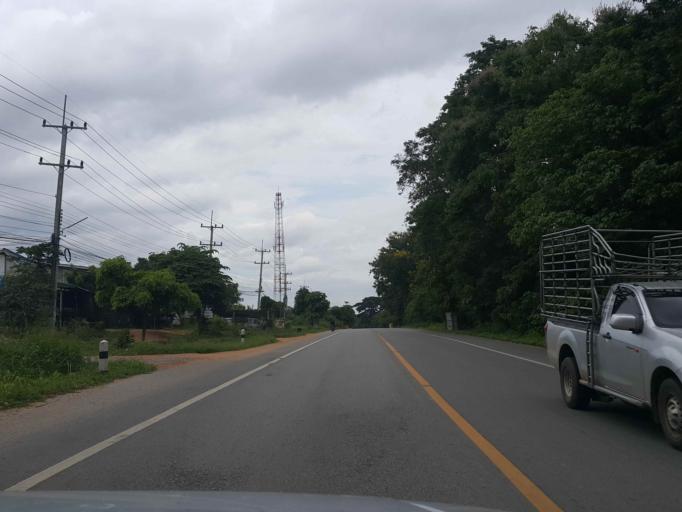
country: TH
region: Lamphun
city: Li
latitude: 17.7900
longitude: 98.9528
